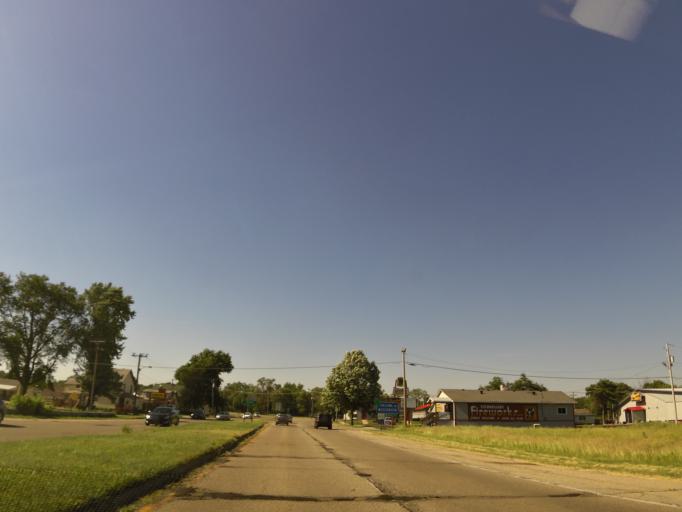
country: US
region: Illinois
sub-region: Winnebago County
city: South Beloit
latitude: 42.4954
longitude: -89.0199
